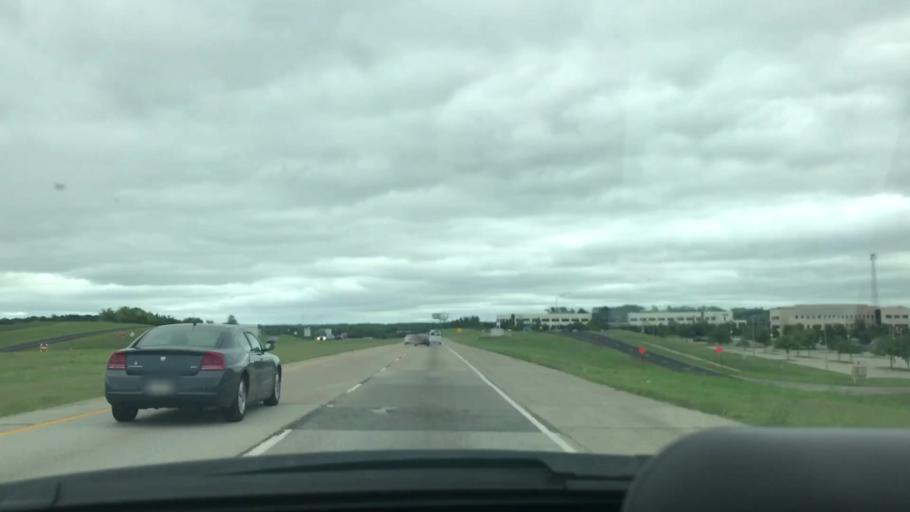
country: US
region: Texas
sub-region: Grayson County
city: Denison
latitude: 33.7086
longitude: -96.5892
